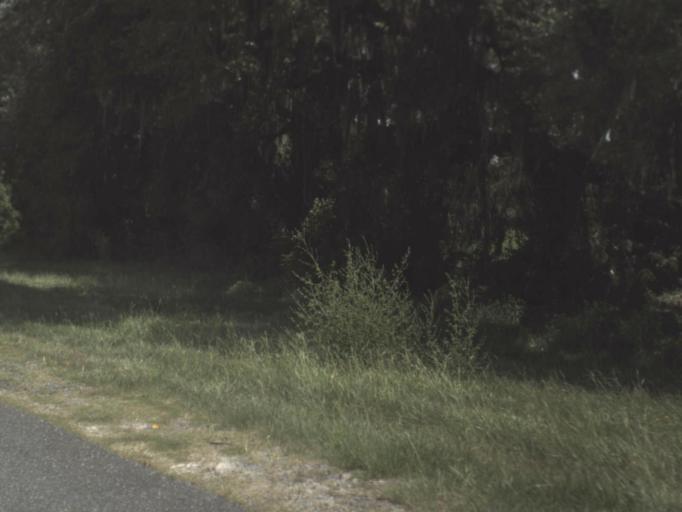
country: US
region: Florida
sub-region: Columbia County
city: Watertown
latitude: 30.1211
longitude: -82.6191
